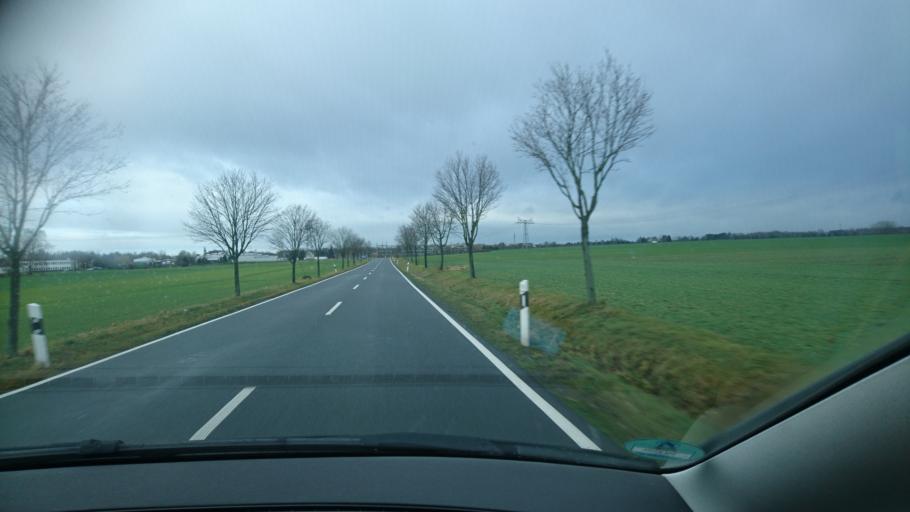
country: DE
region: Saxony
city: Bad Duben
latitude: 51.5883
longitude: 12.6129
